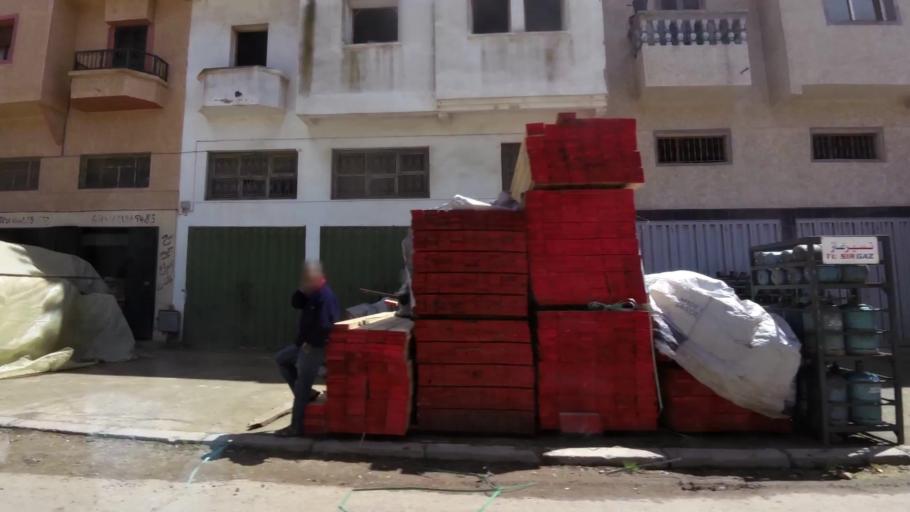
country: MA
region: Grand Casablanca
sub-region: Nouaceur
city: Dar Bouazza
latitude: 33.4163
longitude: -7.8514
